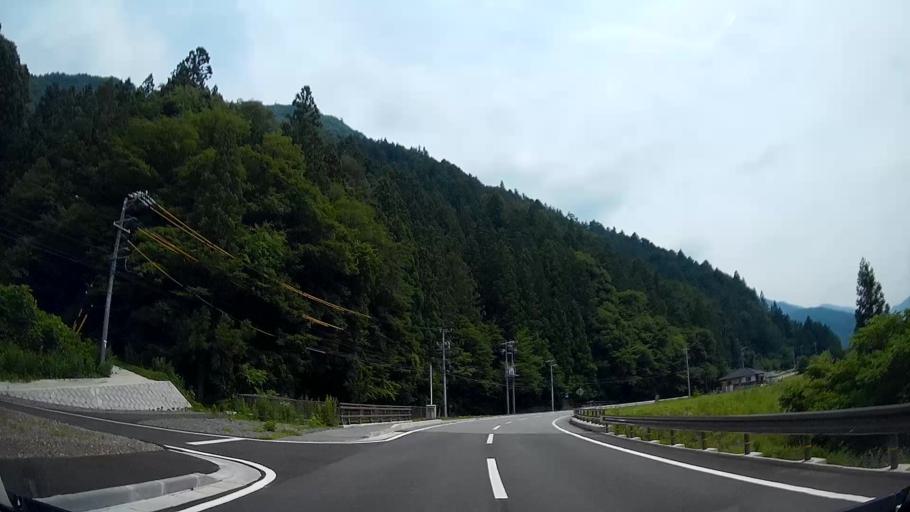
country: JP
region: Nagano
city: Iida
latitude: 35.3134
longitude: 137.9274
